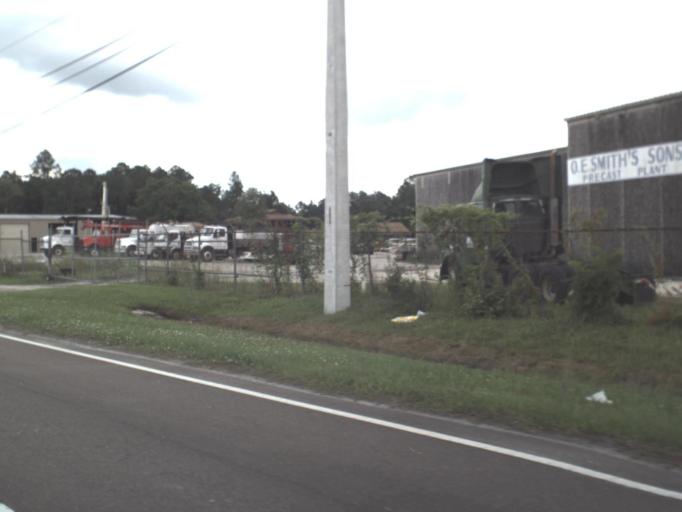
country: US
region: Florida
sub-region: Nassau County
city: Nassau Village-Ratliff
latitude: 30.4478
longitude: -81.7682
